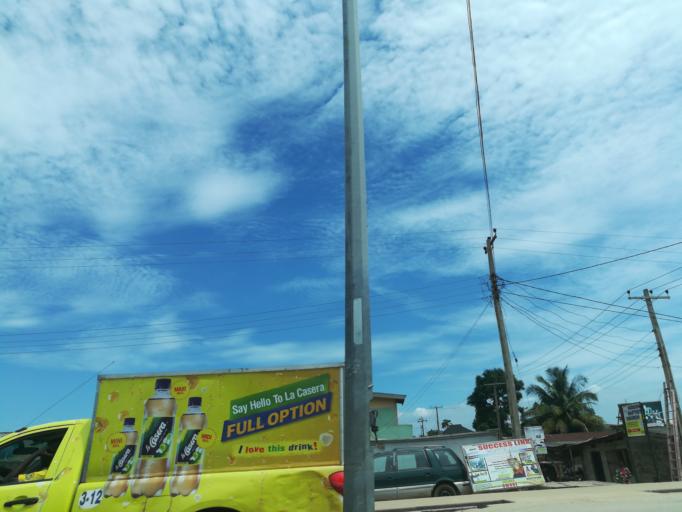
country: NG
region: Lagos
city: Ebute Ikorodu
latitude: 6.5663
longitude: 3.4780
